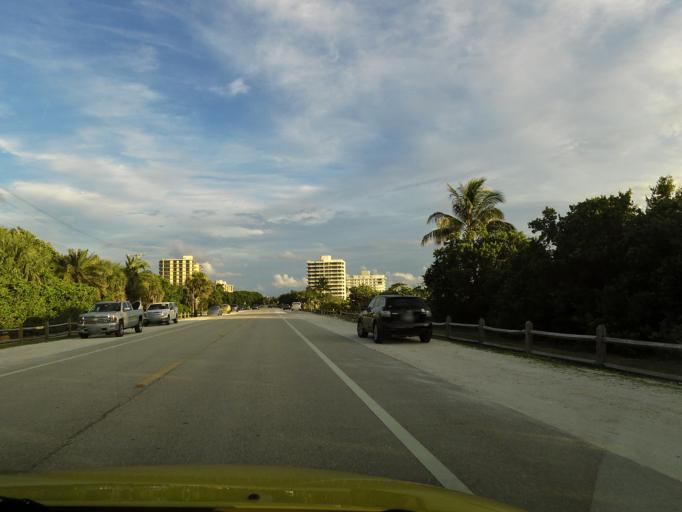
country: US
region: Florida
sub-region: Palm Beach County
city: Jupiter
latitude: 26.9590
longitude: -80.0780
